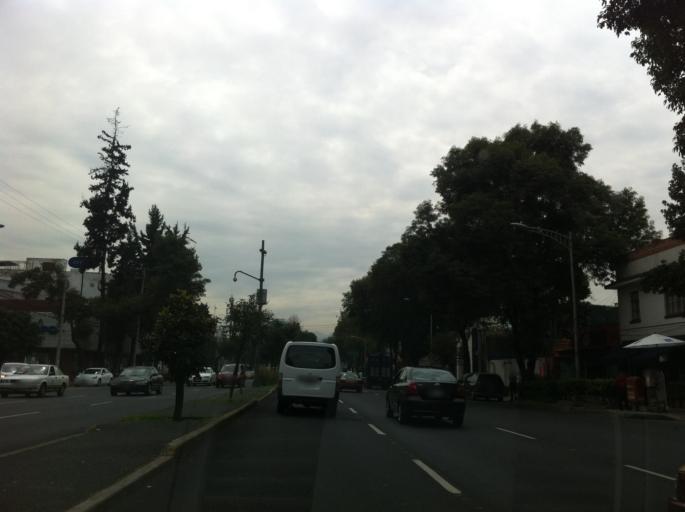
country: MX
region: Mexico City
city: Alvaro Obregon
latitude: 19.3526
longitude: -99.1904
